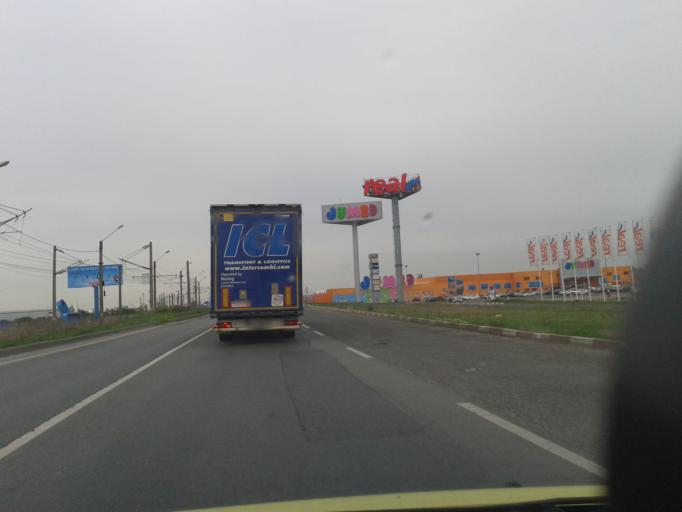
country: RO
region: Arad
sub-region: Comuna Vladimirescu
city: Vladimirescu
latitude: 46.1727
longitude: 21.3780
